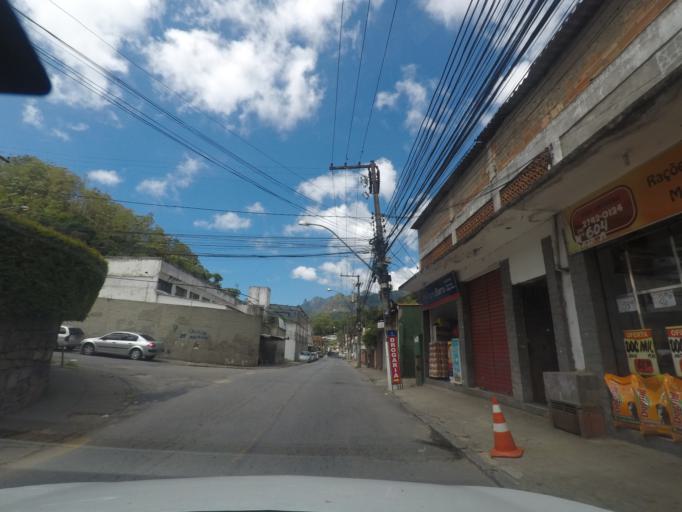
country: BR
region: Rio de Janeiro
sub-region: Teresopolis
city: Teresopolis
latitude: -22.4048
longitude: -42.9771
